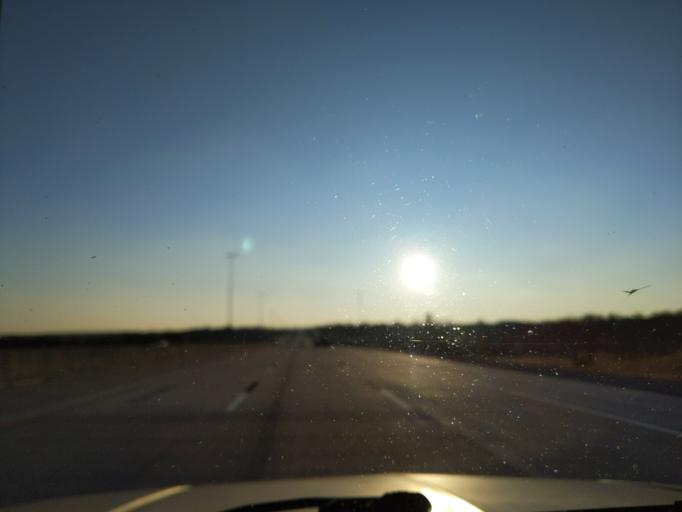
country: US
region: Oklahoma
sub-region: Creek County
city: Kellyville
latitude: 35.9492
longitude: -96.2469
